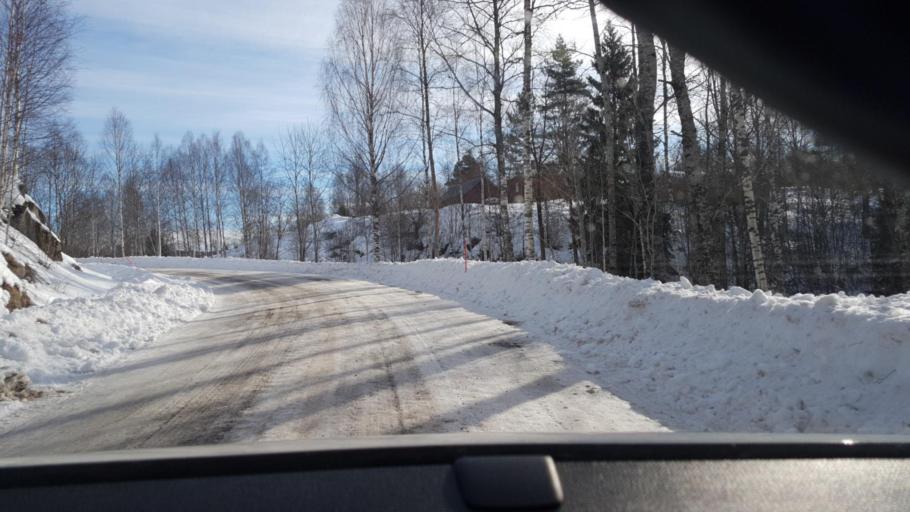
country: NO
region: Hedmark
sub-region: Eidskog
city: Skotterud
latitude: 59.8727
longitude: 11.9751
